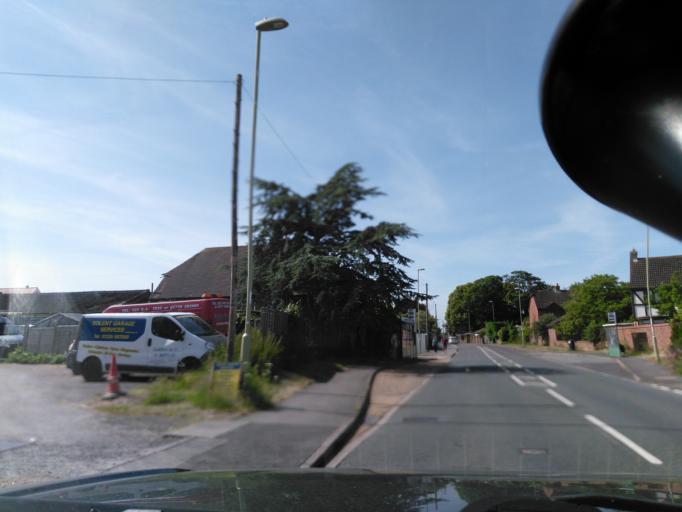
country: GB
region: England
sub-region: Hampshire
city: Lee-on-the-Solent
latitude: 50.8158
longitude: -1.2135
